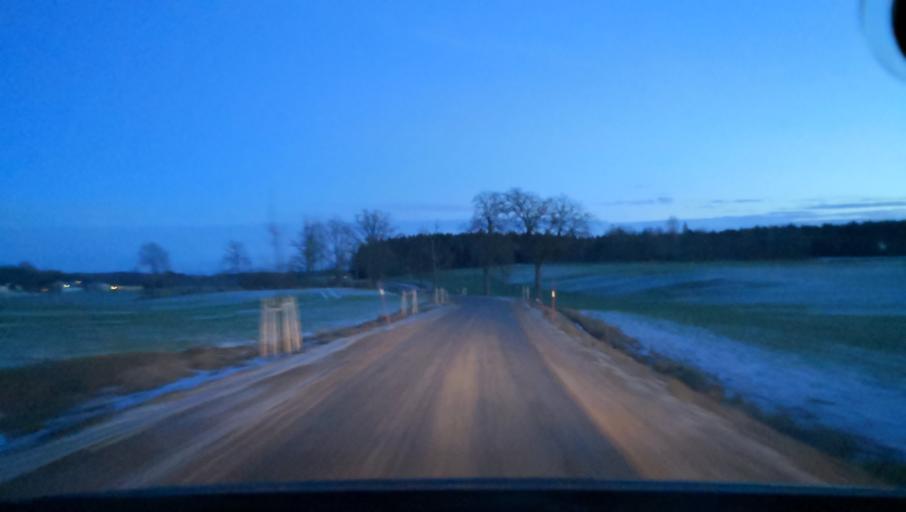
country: SE
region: Soedermanland
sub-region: Katrineholms Kommun
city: Katrineholm
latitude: 59.0685
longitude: 16.3435
